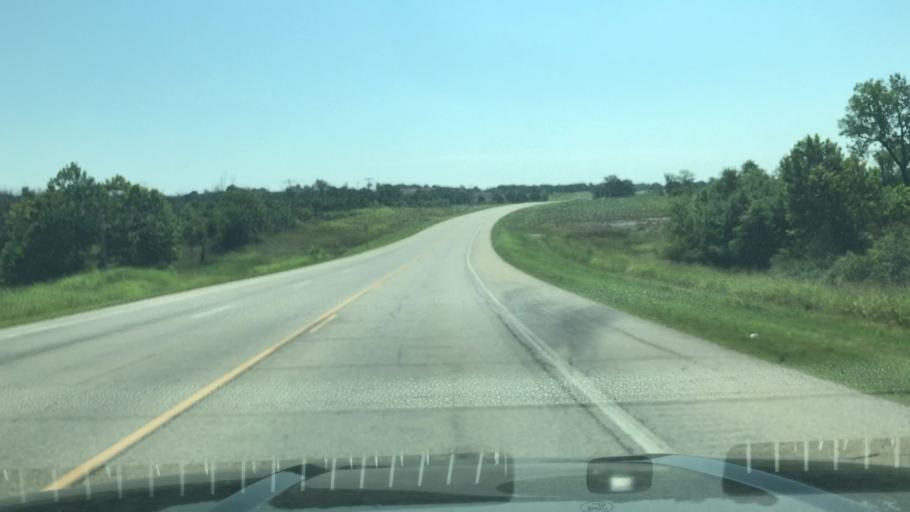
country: US
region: Oklahoma
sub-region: Creek County
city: Mannford
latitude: 36.0031
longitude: -96.3799
